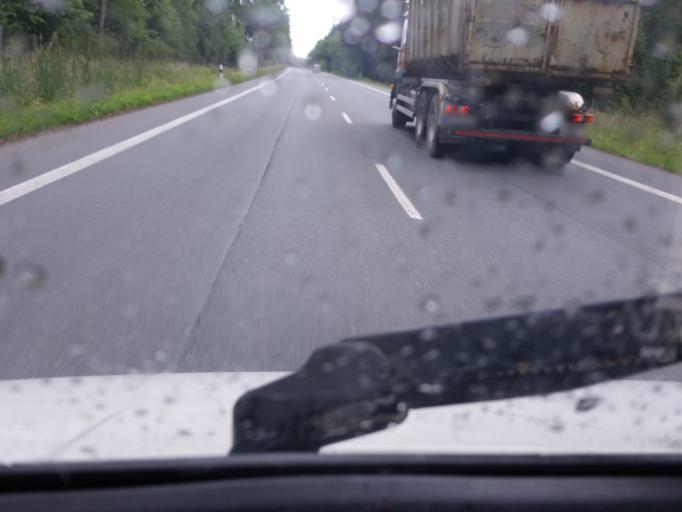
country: DE
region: North Rhine-Westphalia
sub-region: Regierungsbezirk Detmold
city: Petershagen
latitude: 52.3660
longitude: 8.9576
